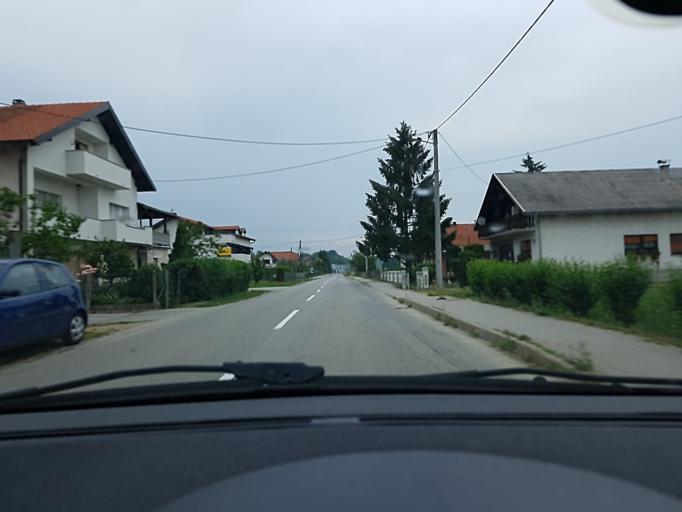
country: HR
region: Zagrebacka
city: Pojatno
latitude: 45.9361
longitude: 15.8135
